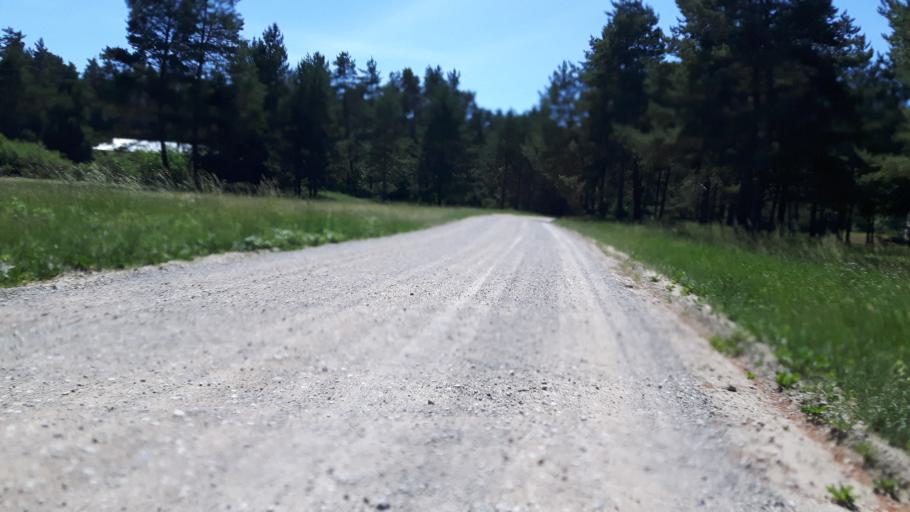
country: LV
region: Kandava
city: Kandava
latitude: 57.0369
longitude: 22.8011
